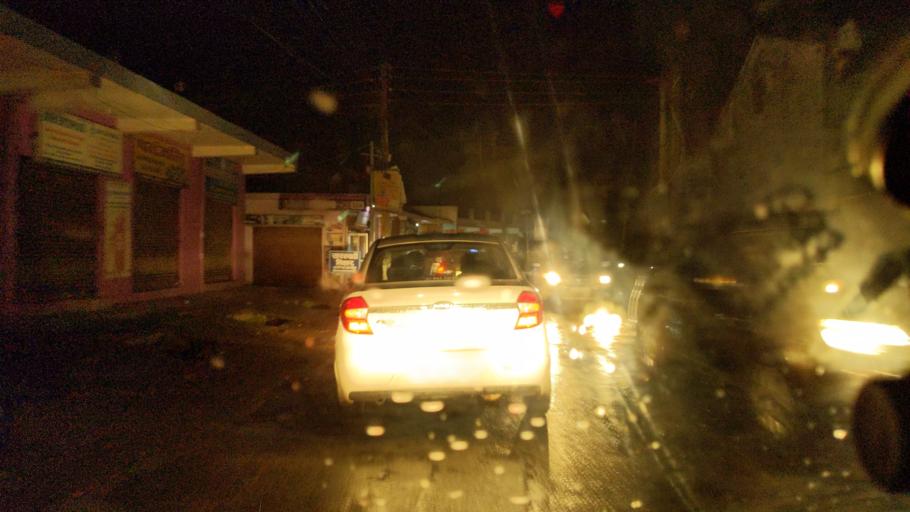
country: IN
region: Uttarakhand
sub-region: Naini Tal
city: Haldwani
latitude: 29.2053
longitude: 79.5063
